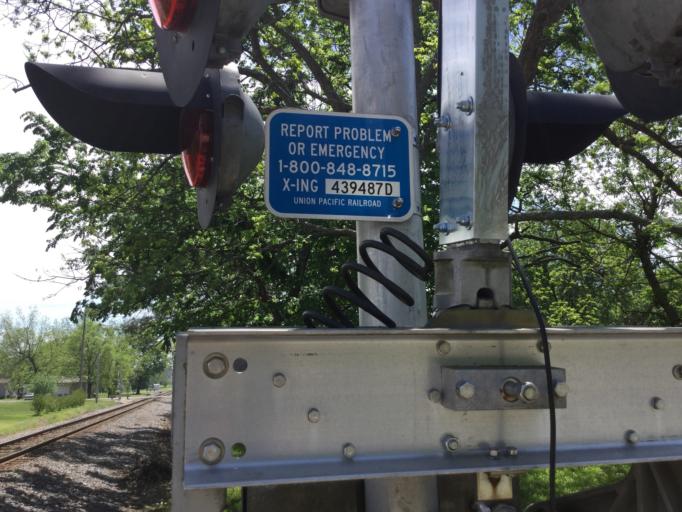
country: US
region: Kansas
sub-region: Coffey County
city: Burlington
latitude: 38.0865
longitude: -95.6310
